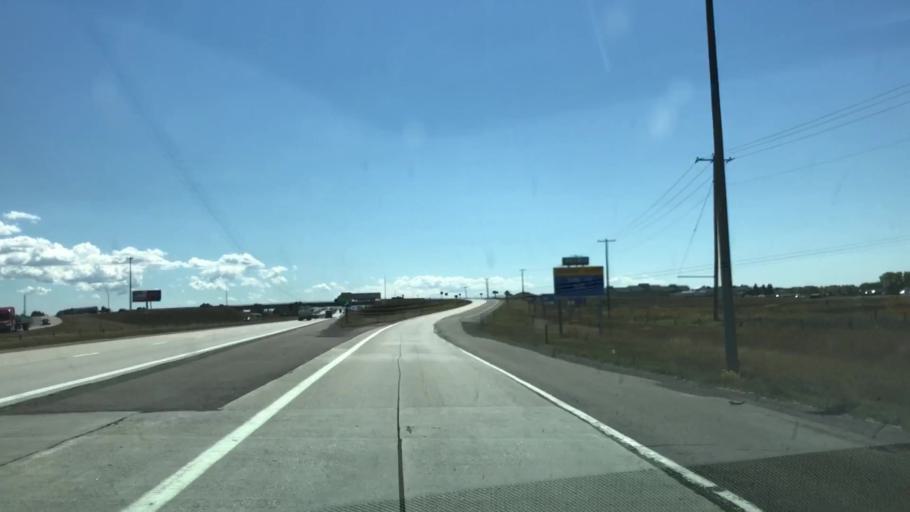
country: US
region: Wyoming
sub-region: Albany County
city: Laramie
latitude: 41.3315
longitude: -105.6164
